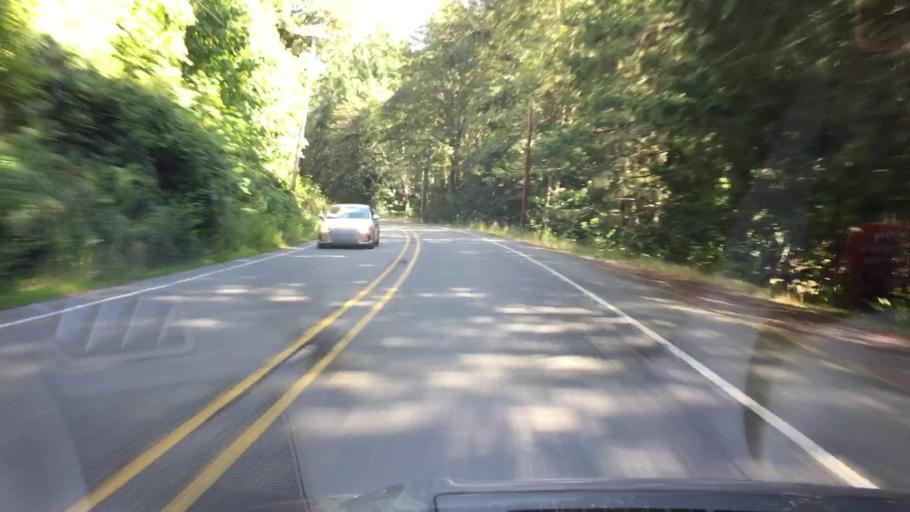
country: US
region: Washington
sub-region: Pierce County
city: Eatonville
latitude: 46.7559
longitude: -121.9720
